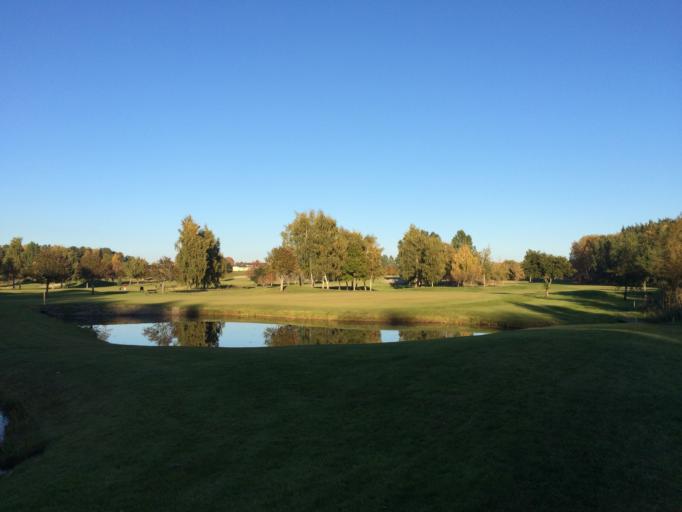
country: SE
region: Stockholm
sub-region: Upplands Vasby Kommun
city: Upplands Vaesby
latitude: 59.4663
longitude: 17.8953
